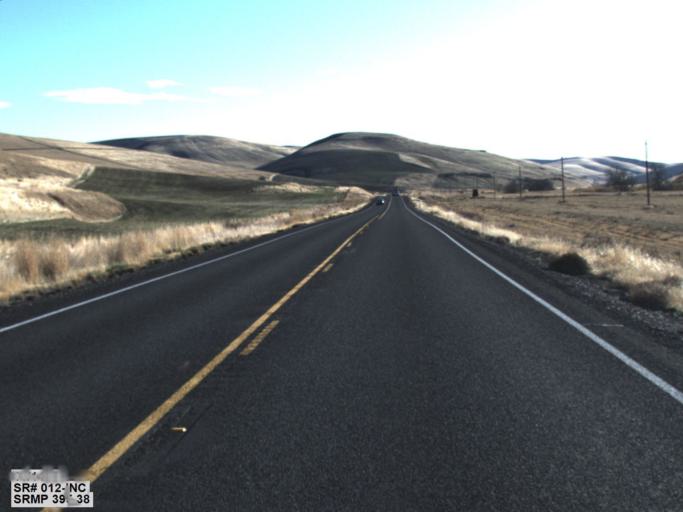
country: US
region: Washington
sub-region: Garfield County
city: Pomeroy
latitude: 46.4862
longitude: -117.7516
